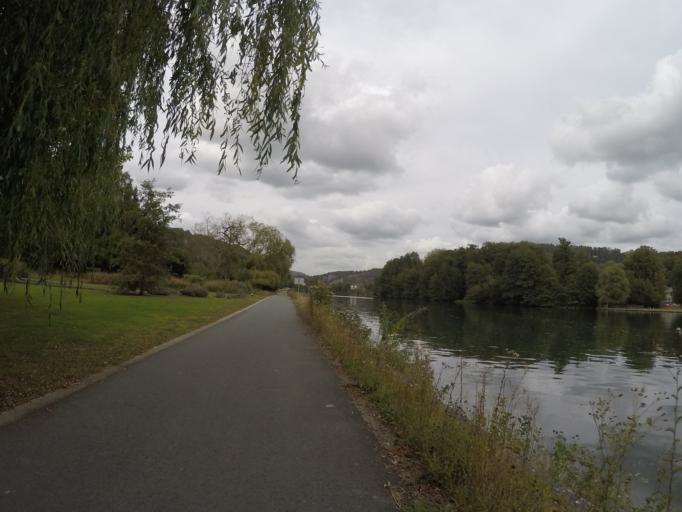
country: BE
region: Wallonia
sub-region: Province de Namur
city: Yvoir
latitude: 50.3208
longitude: 4.8748
